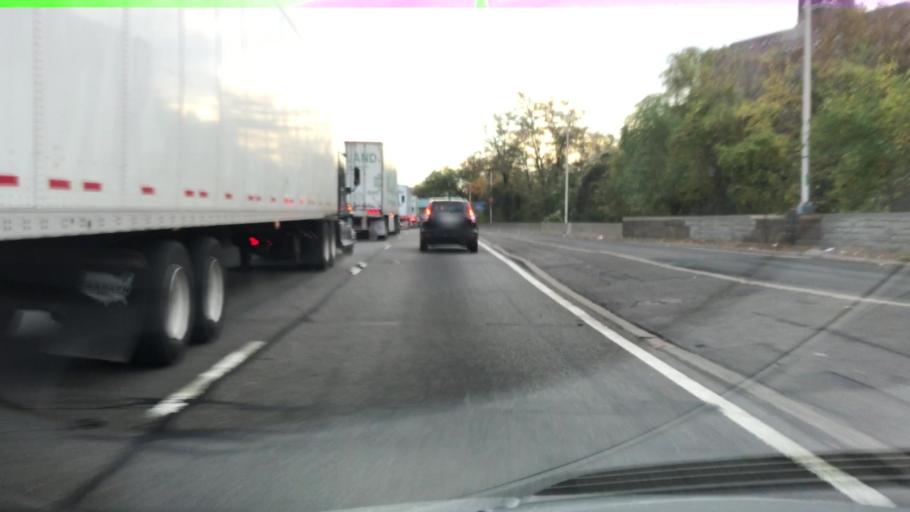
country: US
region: New York
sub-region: New York County
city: Inwood
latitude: 40.8753
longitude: -73.9051
